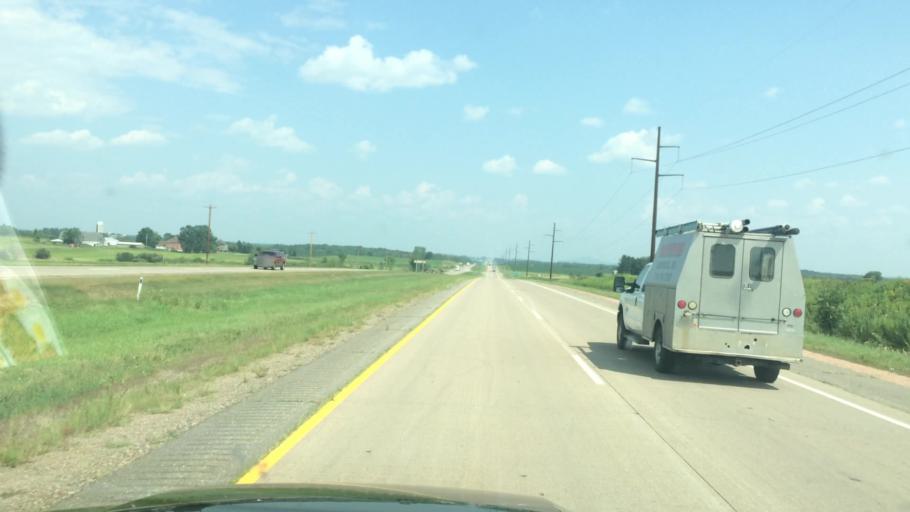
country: US
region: Wisconsin
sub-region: Marathon County
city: Edgar
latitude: 44.9441
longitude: -90.0031
